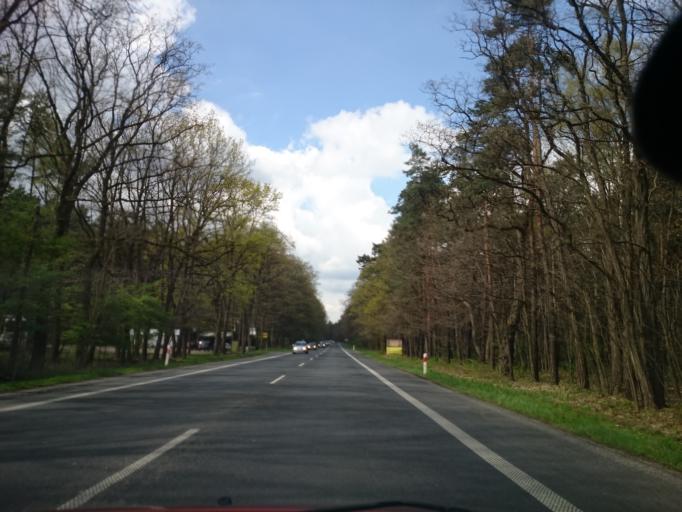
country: PL
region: Opole Voivodeship
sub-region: Powiat opolski
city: Tarnow Opolski
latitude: 50.6182
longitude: 18.0611
